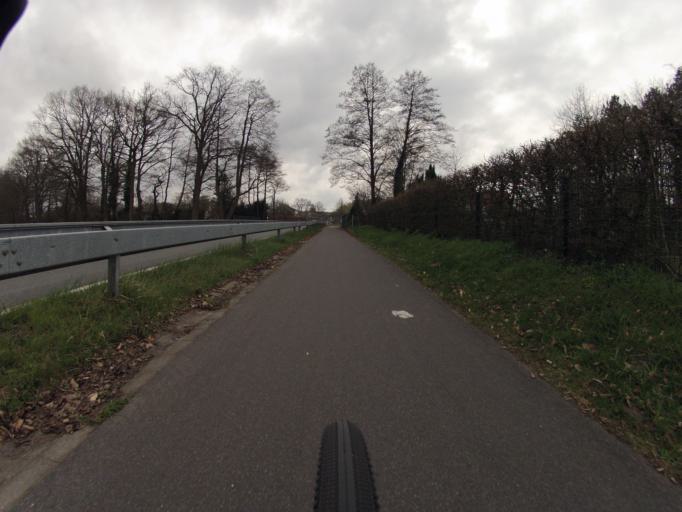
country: DE
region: North Rhine-Westphalia
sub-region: Regierungsbezirk Munster
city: Recke
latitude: 52.3519
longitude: 7.7153
